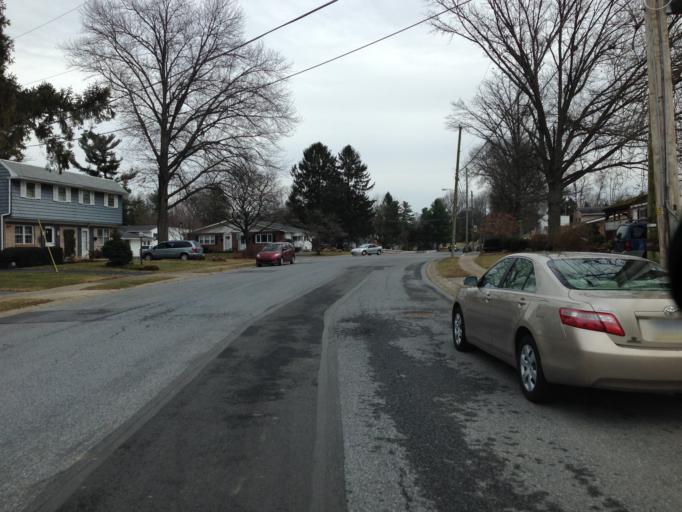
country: US
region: Pennsylvania
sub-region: Lancaster County
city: Lititz
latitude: 40.1487
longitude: -76.3149
